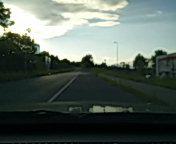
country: HU
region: Pest
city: Toeroekbalint
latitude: 47.4457
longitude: 18.8845
